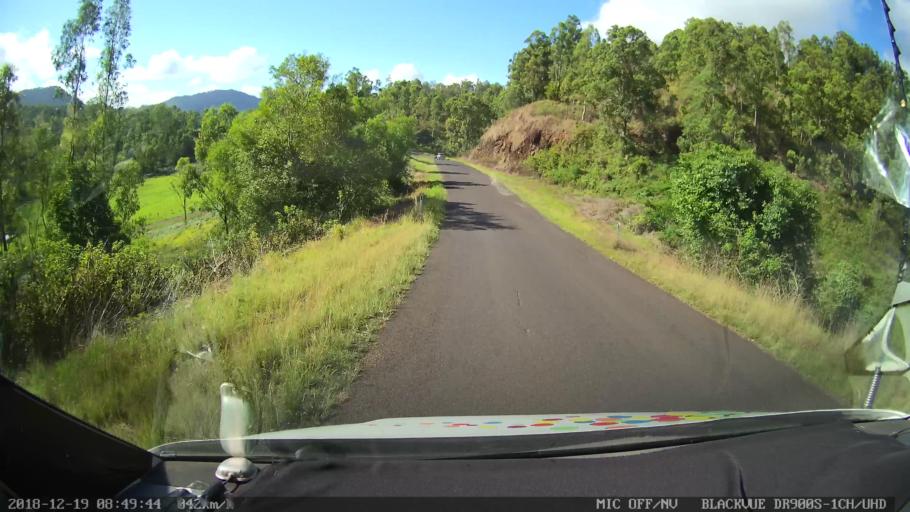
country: AU
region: New South Wales
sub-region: Kyogle
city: Kyogle
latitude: -28.3769
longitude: 152.9731
